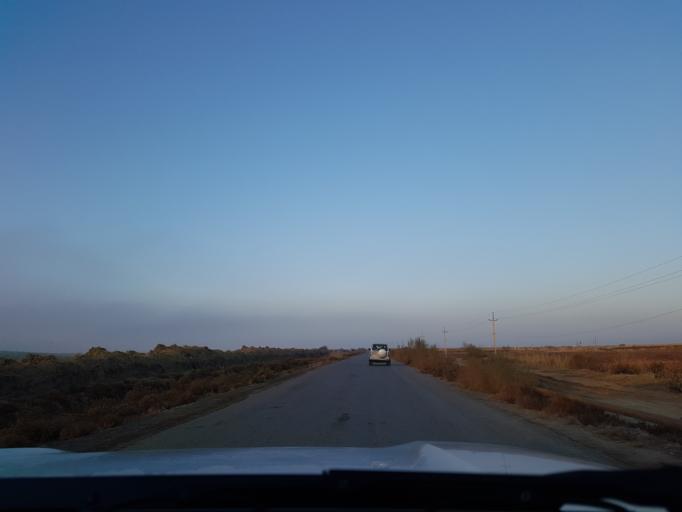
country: TM
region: Dasoguz
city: Koeneuergench
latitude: 41.8441
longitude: 58.6473
